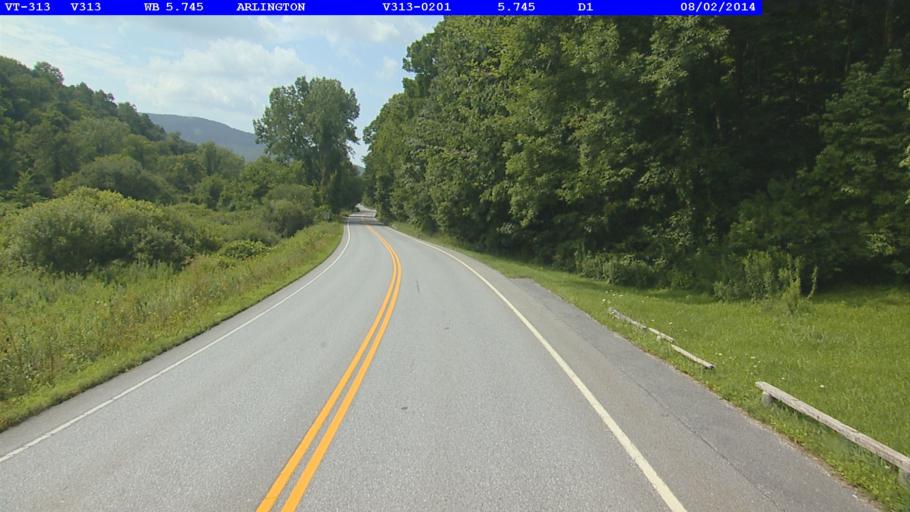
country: US
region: Vermont
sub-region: Bennington County
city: Arlington
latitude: 43.0789
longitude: -73.1689
